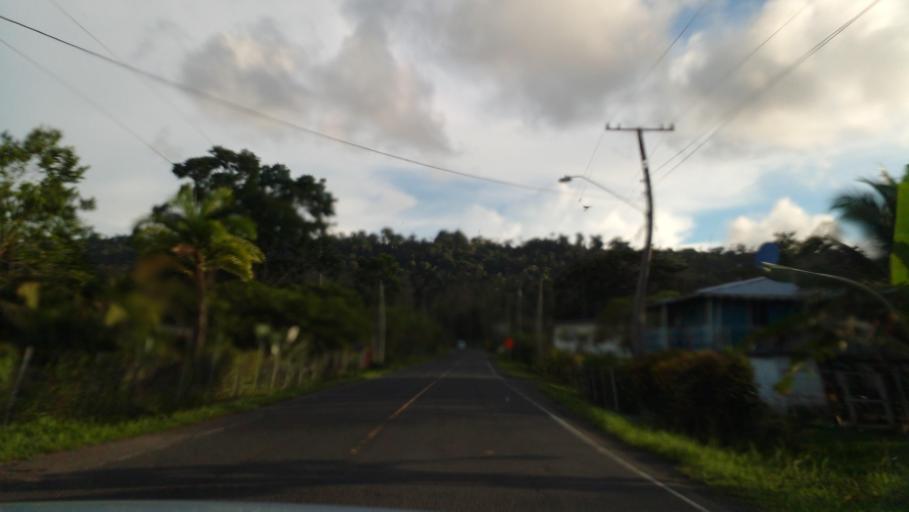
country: PA
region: Bocas del Toro
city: Almirante
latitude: 9.2819
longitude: -82.4137
